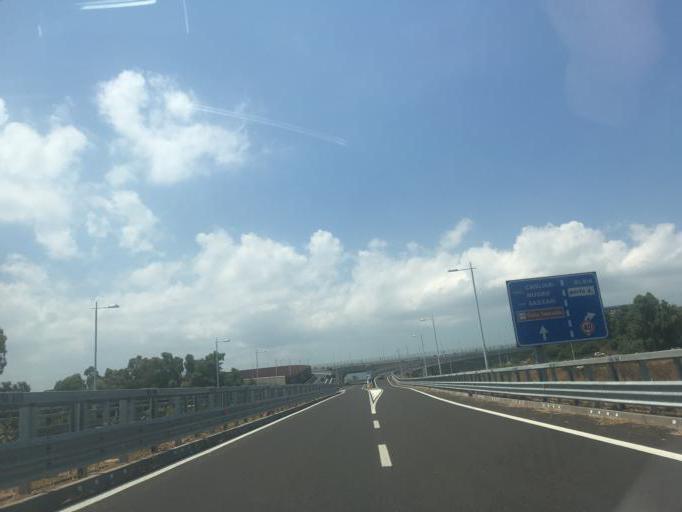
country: IT
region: Sardinia
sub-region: Provincia di Olbia-Tempio
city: Olbia
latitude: 40.9036
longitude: 9.5052
